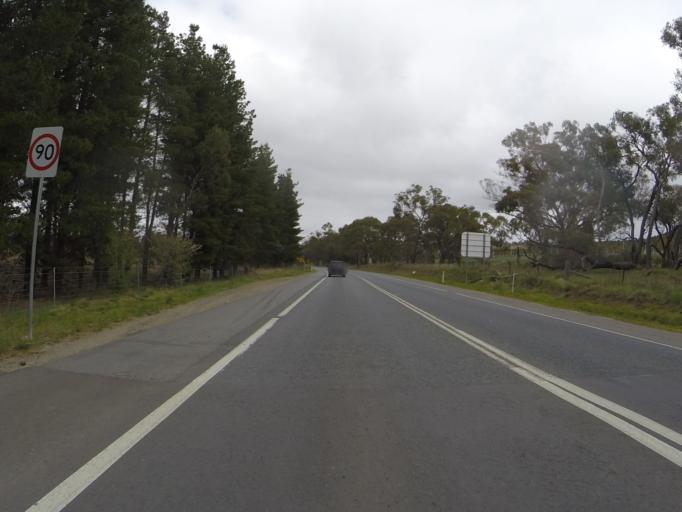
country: AU
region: Australian Capital Territory
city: Canberra
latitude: -35.2448
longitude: 149.1922
